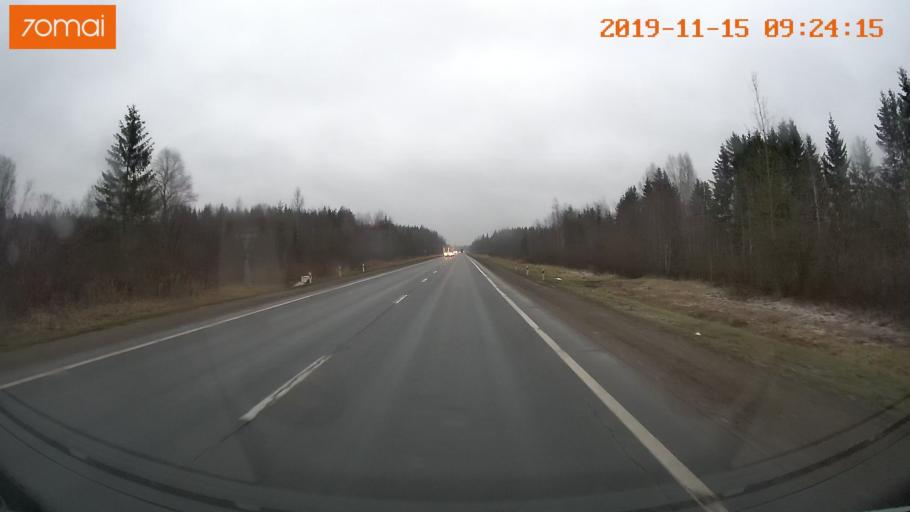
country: RU
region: Vologda
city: Tonshalovo
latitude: 59.3037
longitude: 38.1332
